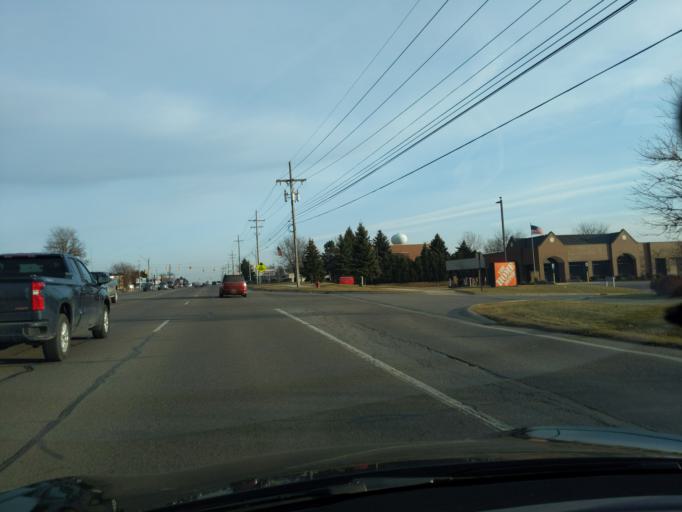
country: US
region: Michigan
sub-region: Livingston County
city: Howell
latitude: 42.5915
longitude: -83.8872
